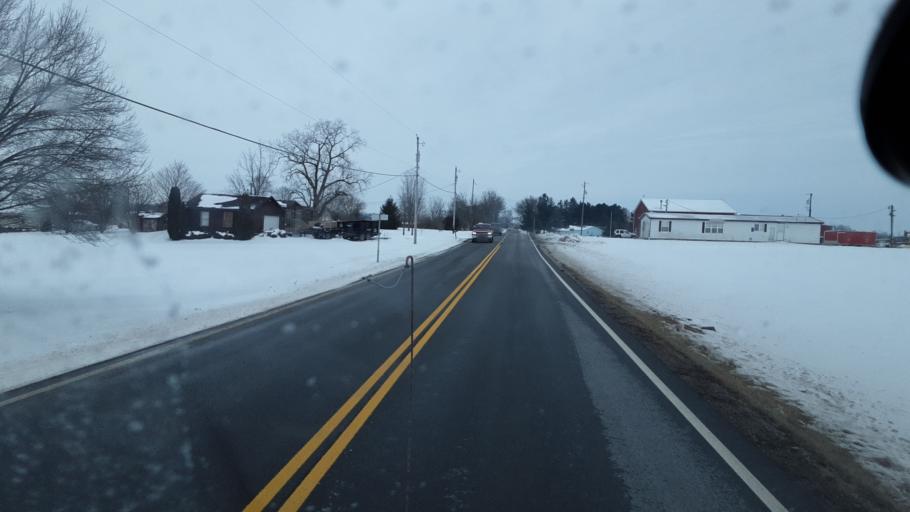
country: US
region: Ohio
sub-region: Union County
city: New California
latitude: 40.2127
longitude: -83.2435
